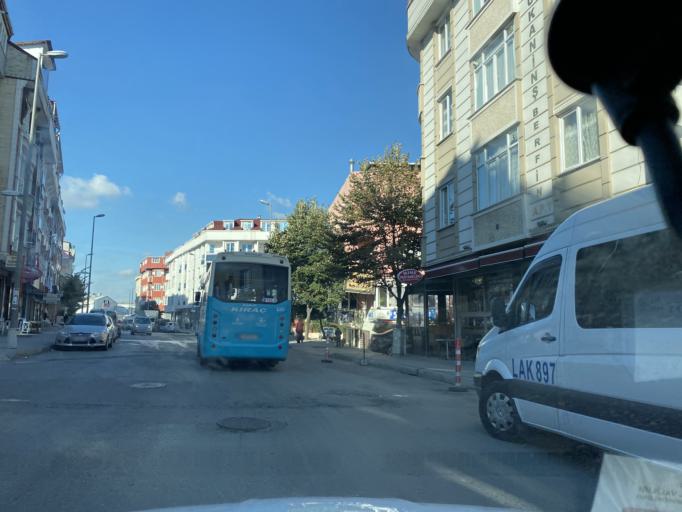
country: TR
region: Istanbul
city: Esenyurt
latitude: 41.0441
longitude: 28.6508
